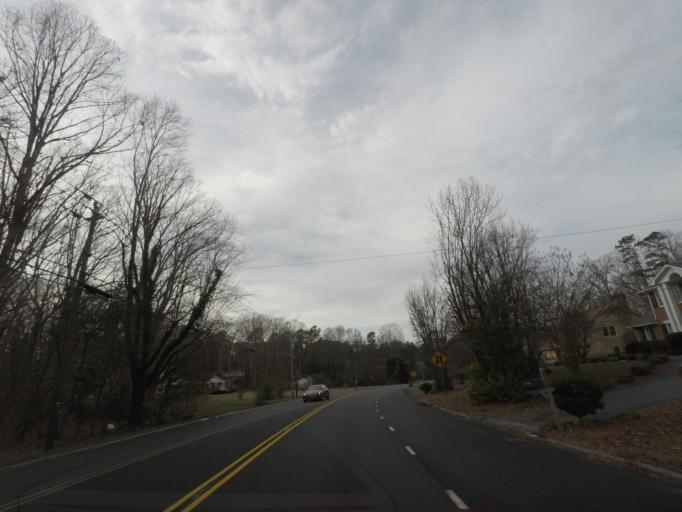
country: US
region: North Carolina
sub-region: Durham County
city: Durham
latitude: 36.0413
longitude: -78.9594
